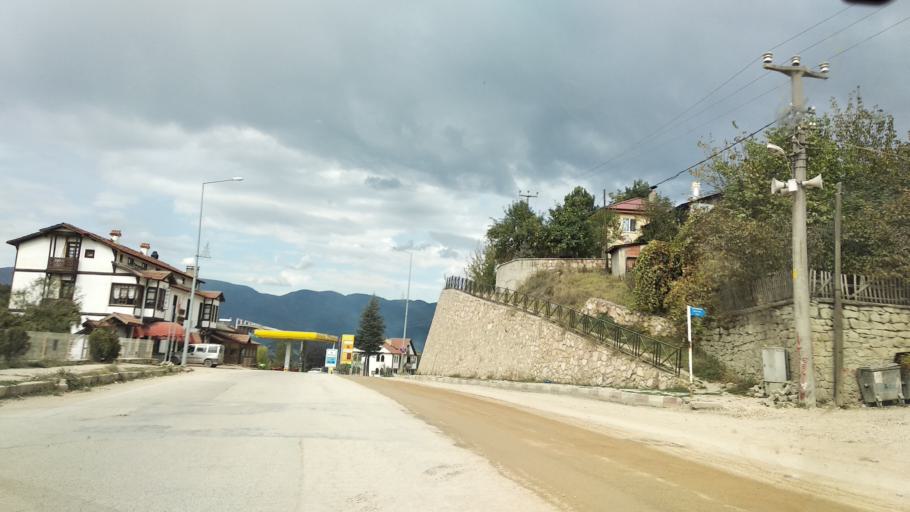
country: TR
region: Bolu
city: Mudurnu
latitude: 40.4726
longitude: 31.2098
